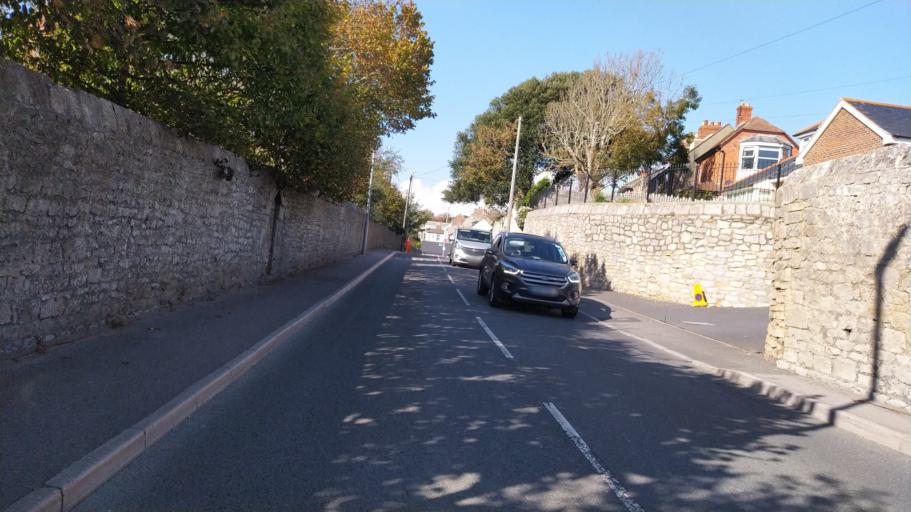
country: GB
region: England
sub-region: Dorset
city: Weymouth
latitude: 50.5972
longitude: -2.4773
